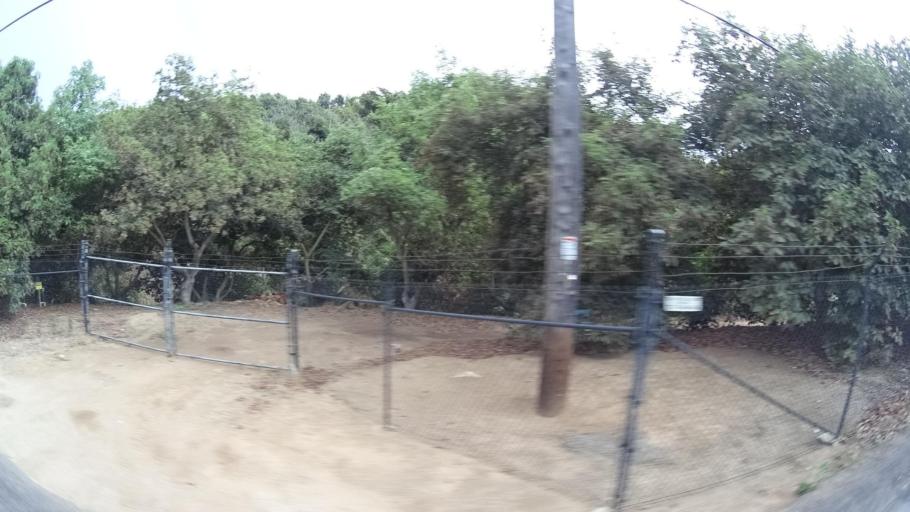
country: US
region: California
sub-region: San Diego County
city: San Pasqual
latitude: 33.0453
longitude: -116.9735
